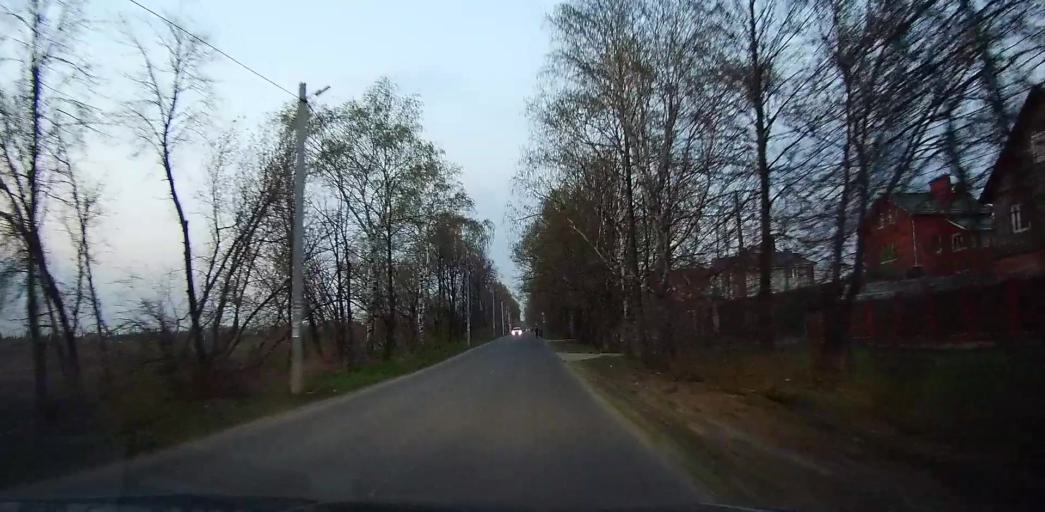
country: RU
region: Moskovskaya
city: Ramenskoye
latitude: 55.5736
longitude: 38.2975
